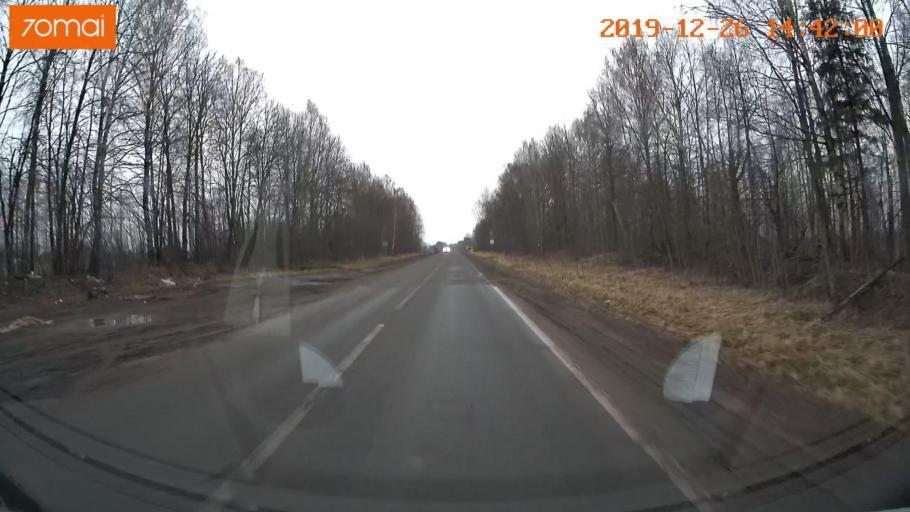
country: RU
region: Jaroslavl
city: Poshekhon'ye
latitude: 58.3670
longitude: 39.0257
